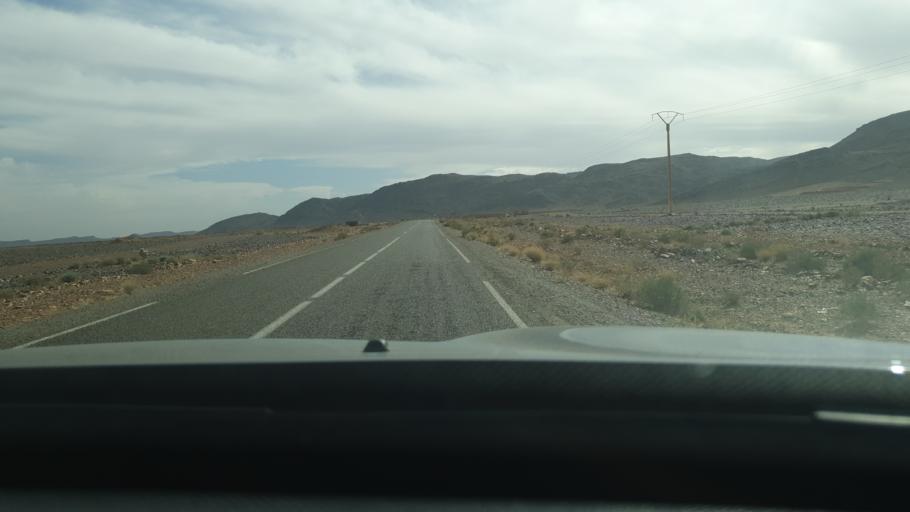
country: MA
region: Meknes-Tafilalet
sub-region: Errachidia
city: Fezna
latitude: 31.5321
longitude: -4.6408
